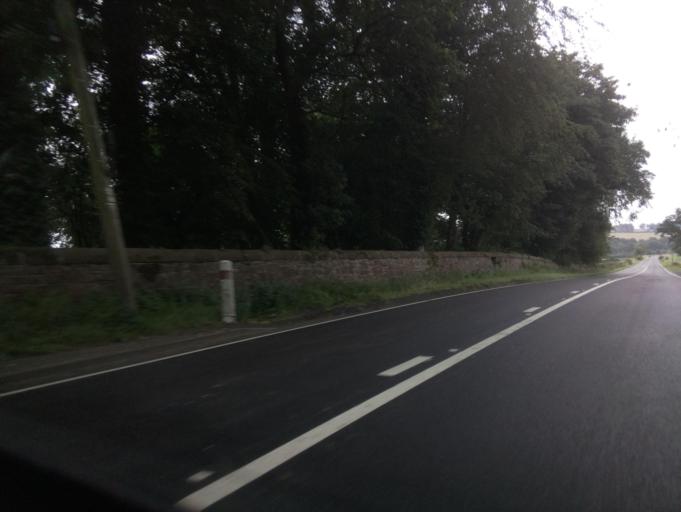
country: GB
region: Scotland
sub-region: Dumfries and Galloway
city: Locharbriggs
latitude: 55.1718
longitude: -3.5448
